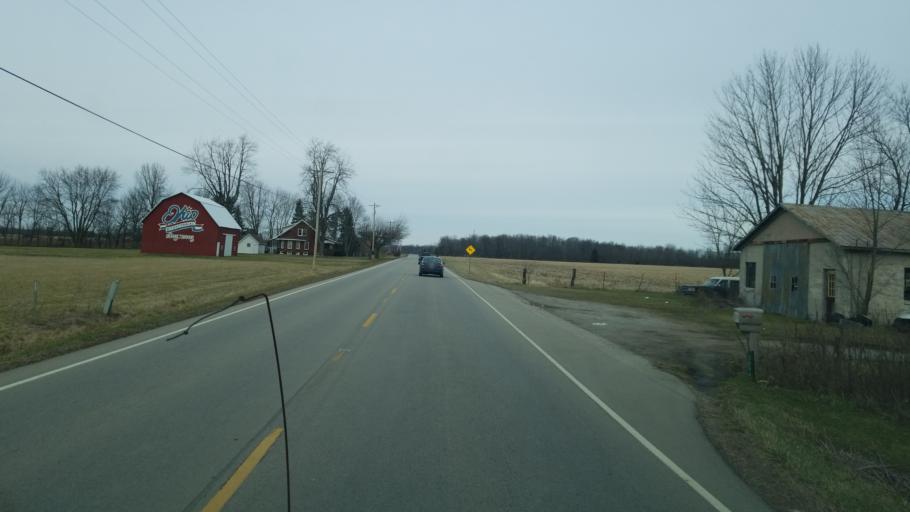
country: US
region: Ohio
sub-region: Highland County
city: Hillsboro
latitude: 39.0936
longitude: -83.6804
